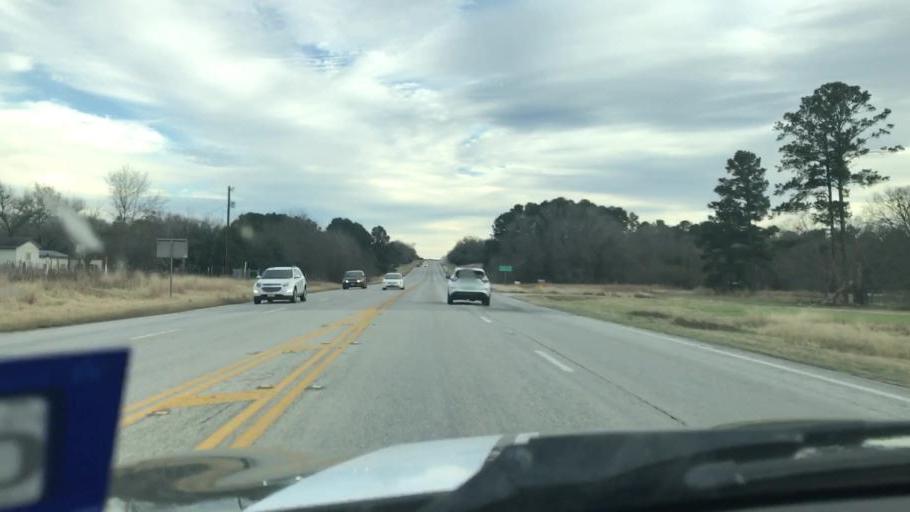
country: US
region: Texas
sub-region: Bastrop County
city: Camp Swift
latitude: 30.2777
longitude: -97.2411
